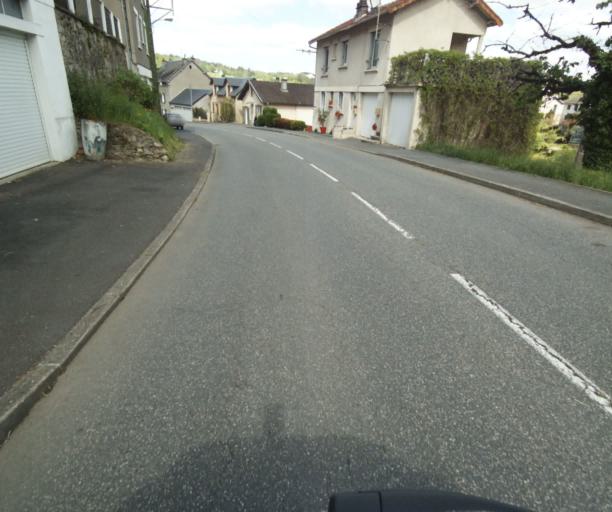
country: FR
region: Limousin
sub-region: Departement de la Correze
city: Tulle
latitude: 45.2682
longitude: 1.7784
